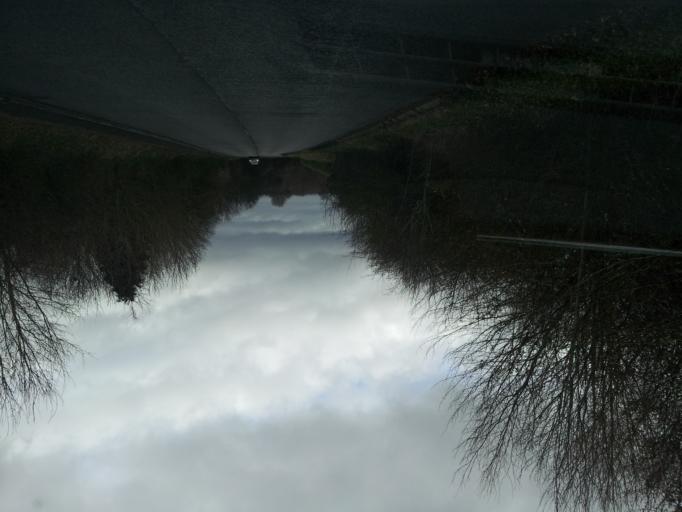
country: GB
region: England
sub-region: Somerset
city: Stoke-sub-Hamdon
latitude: 50.9543
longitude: -2.7234
